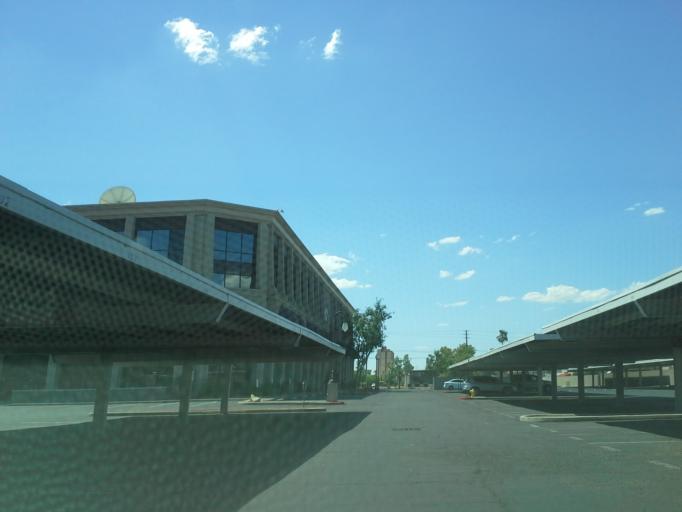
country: US
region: Arizona
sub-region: Maricopa County
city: Phoenix
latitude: 33.5075
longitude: -112.0631
